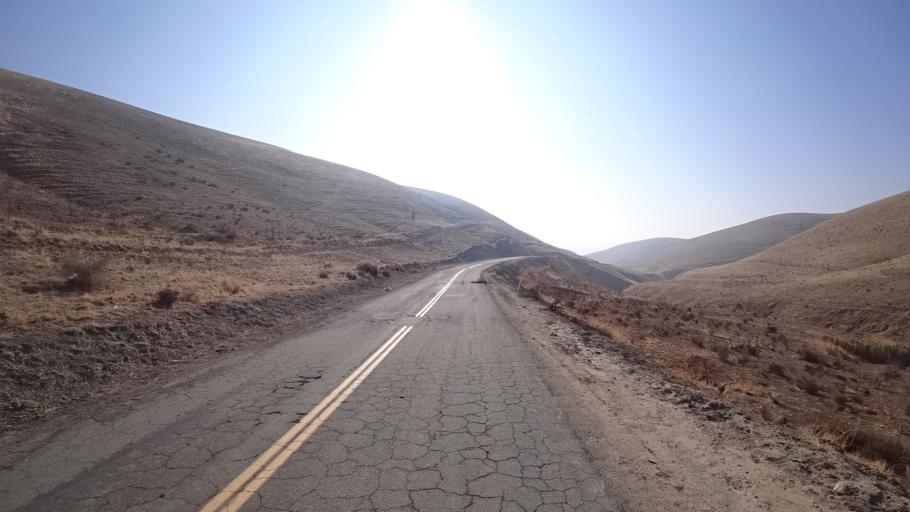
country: US
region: California
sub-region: Kern County
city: Oildale
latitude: 35.4529
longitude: -118.8278
